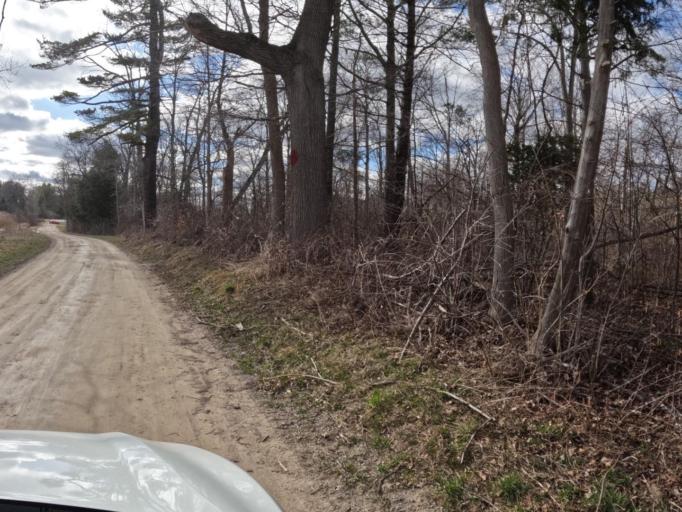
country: CA
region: Ontario
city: Norfolk County
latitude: 42.7647
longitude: -80.3006
